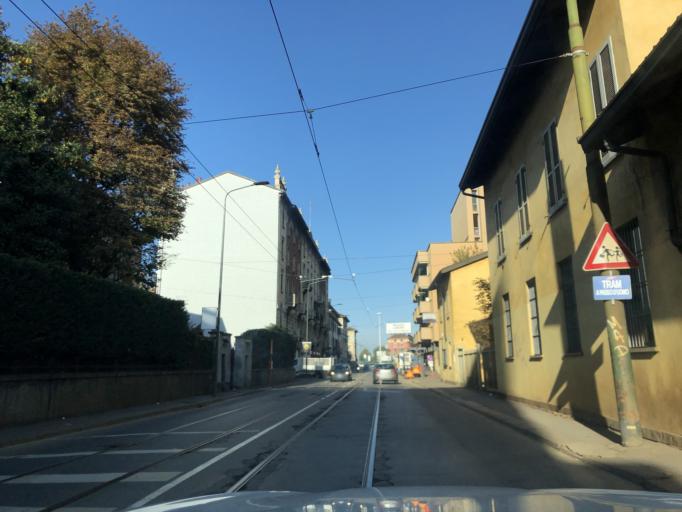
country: IT
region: Lombardy
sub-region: Citta metropolitana di Milano
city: Novate Milanese
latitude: 45.5095
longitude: 9.1316
